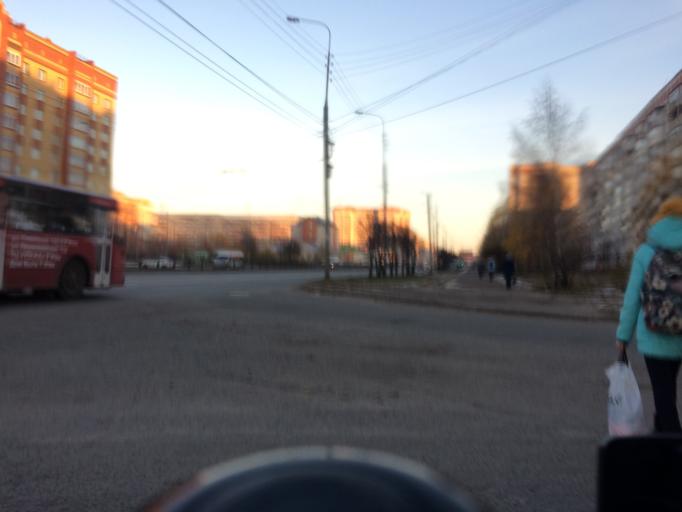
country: RU
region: Mariy-El
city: Yoshkar-Ola
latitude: 56.6364
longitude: 47.9156
